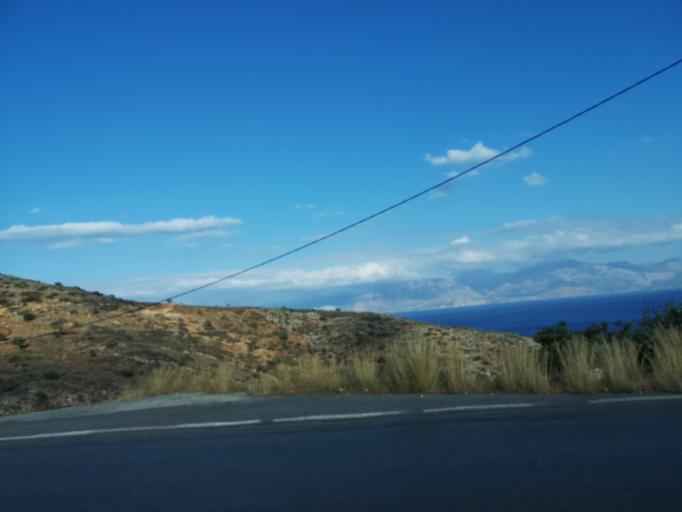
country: GR
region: Crete
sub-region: Nomos Lasithiou
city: Skhisma
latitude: 35.2306
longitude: 25.7236
